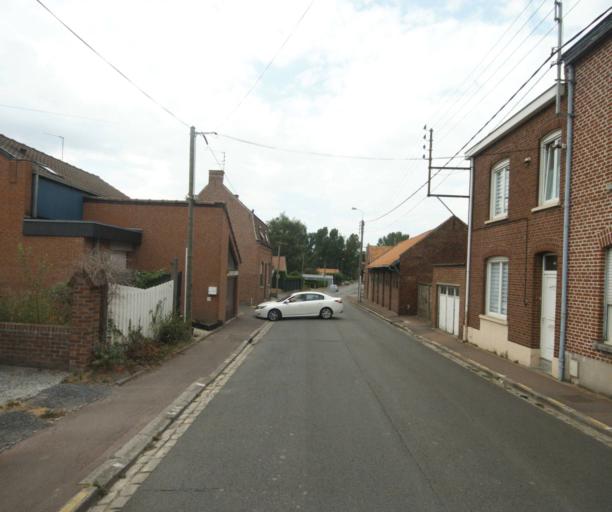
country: FR
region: Nord-Pas-de-Calais
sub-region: Departement du Nord
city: Neuville-en-Ferrain
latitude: 50.7526
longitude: 3.1497
